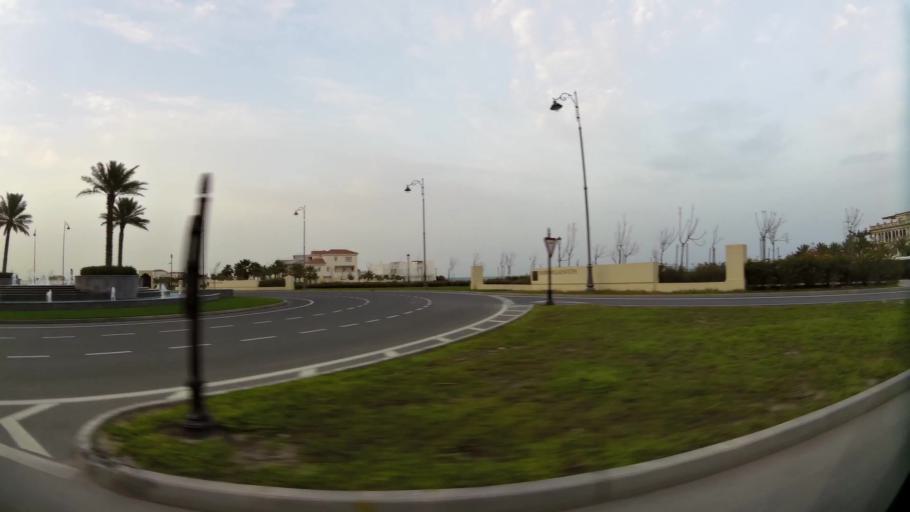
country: QA
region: Baladiyat ad Dawhah
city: Doha
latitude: 25.3691
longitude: 51.5622
